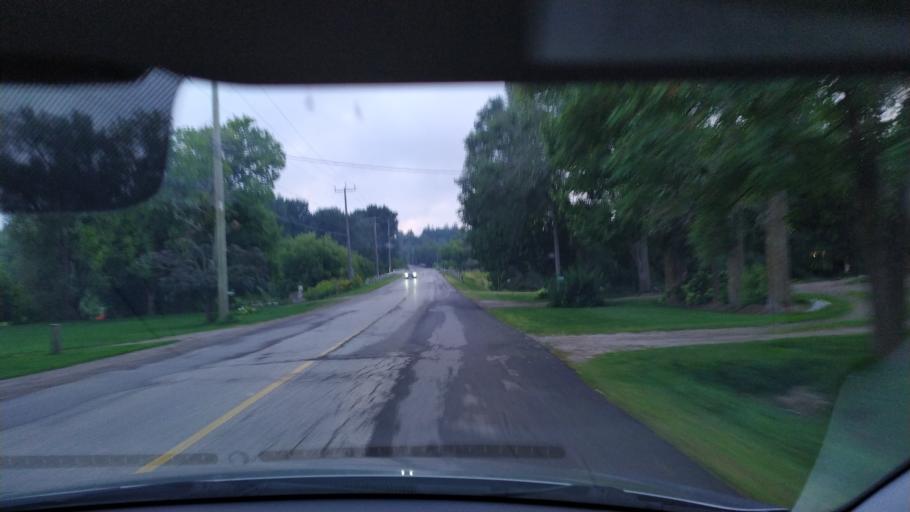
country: CA
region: Ontario
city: Kitchener
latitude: 43.3556
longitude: -80.6628
